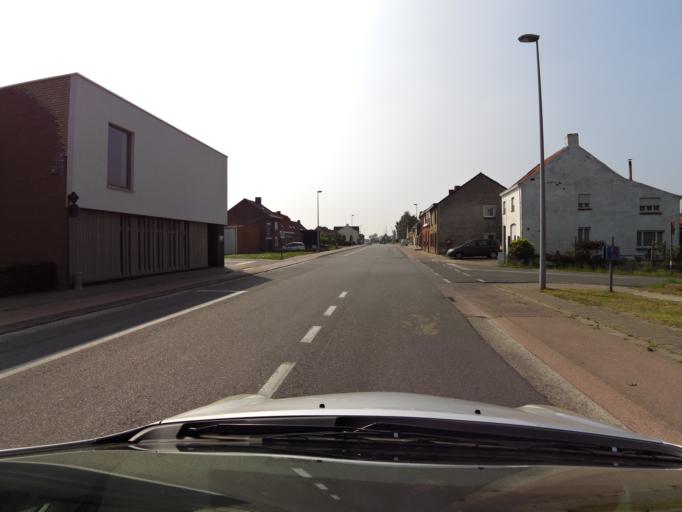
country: BE
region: Flanders
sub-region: Provincie West-Vlaanderen
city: Poperinge
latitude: 50.8559
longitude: 2.7128
